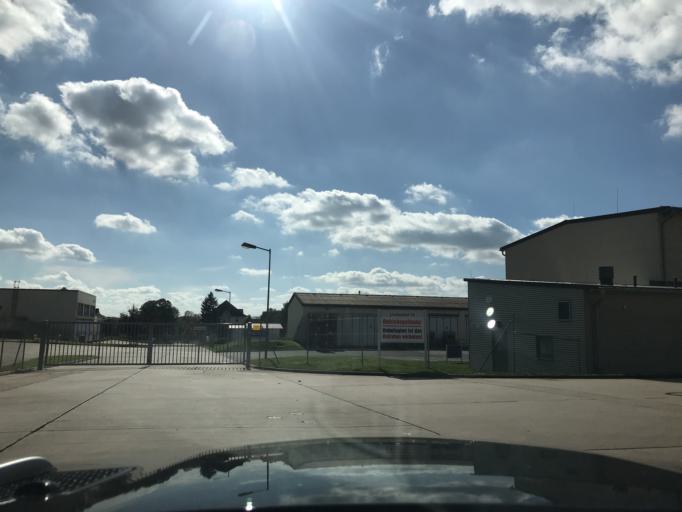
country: DE
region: Thuringia
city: Muehlhausen
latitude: 51.2180
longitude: 10.4820
